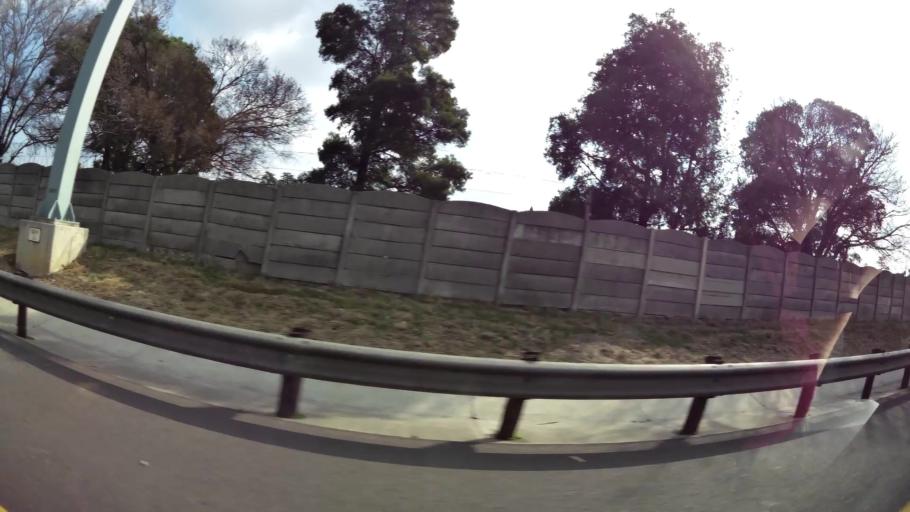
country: ZA
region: Gauteng
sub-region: Ekurhuleni Metropolitan Municipality
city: Benoni
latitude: -26.1783
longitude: 28.3245
